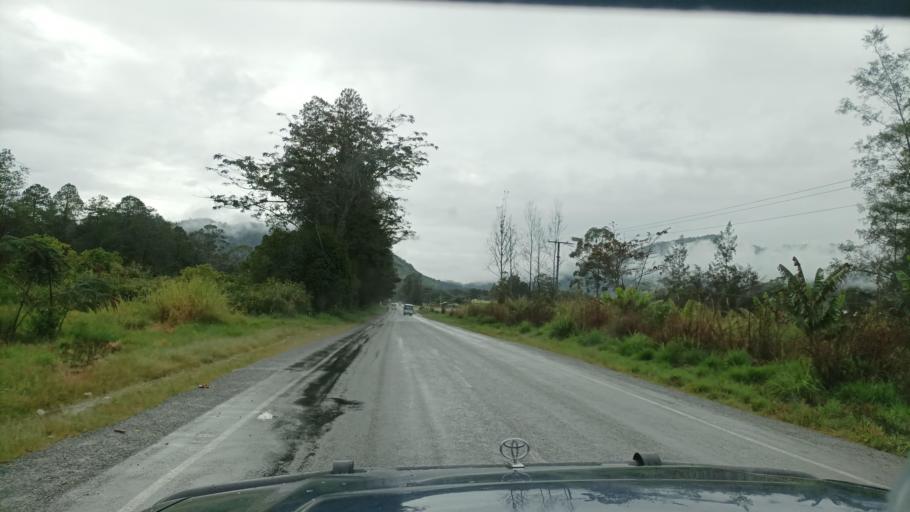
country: PG
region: Western Highlands
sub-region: Hagen
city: Mount Hagen
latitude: -5.8356
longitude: 144.3372
